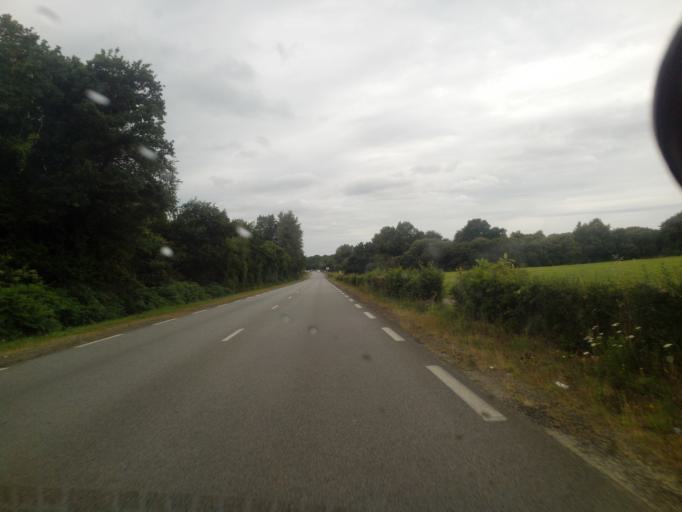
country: FR
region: Brittany
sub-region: Departement du Morbihan
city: Kervignac
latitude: 47.7601
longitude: -3.2585
